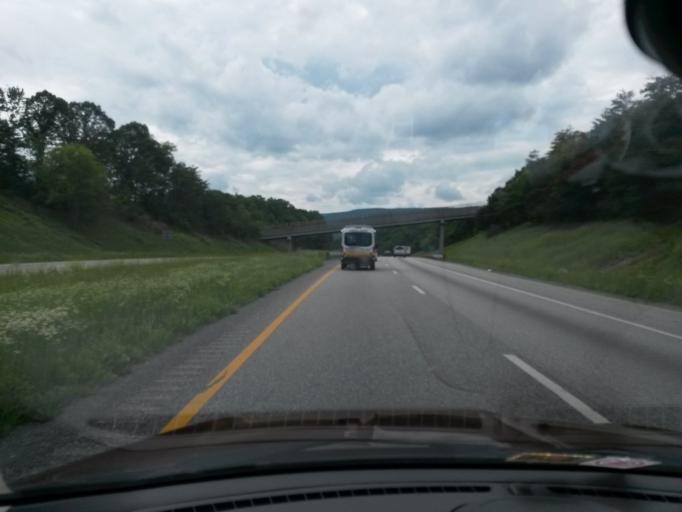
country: US
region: Virginia
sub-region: Alleghany County
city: Clifton Forge
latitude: 37.8297
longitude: -79.8182
